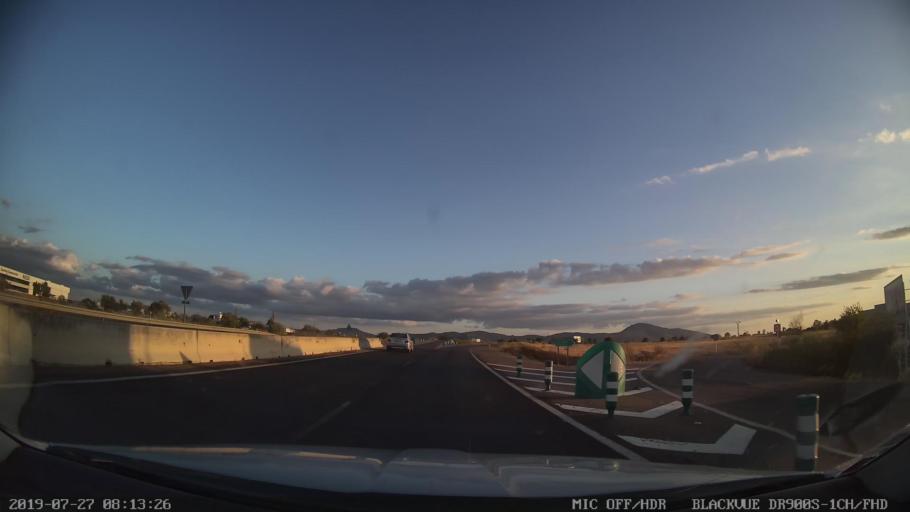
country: ES
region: Extremadura
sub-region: Provincia de Badajoz
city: Calamonte
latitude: 38.9035
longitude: -6.3682
